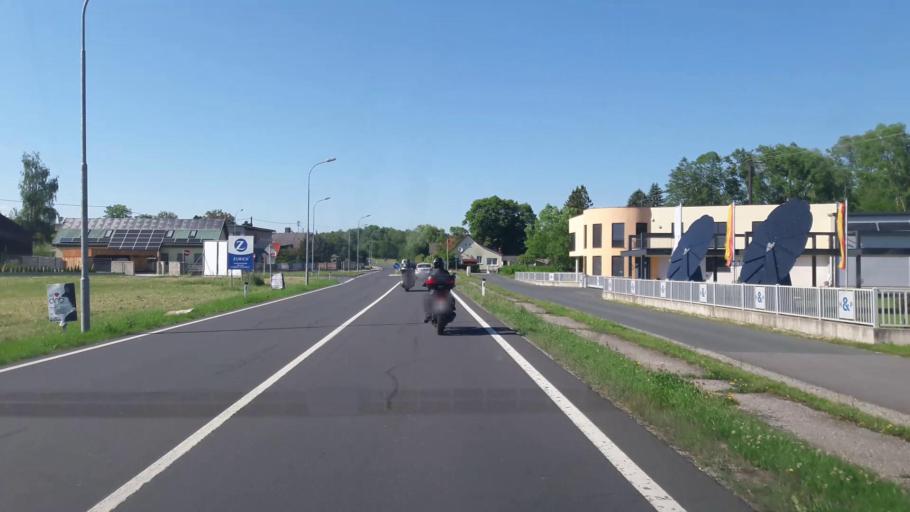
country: AT
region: Burgenland
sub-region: Politischer Bezirk Oberwart
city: Kemeten
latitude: 47.2566
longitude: 16.1538
